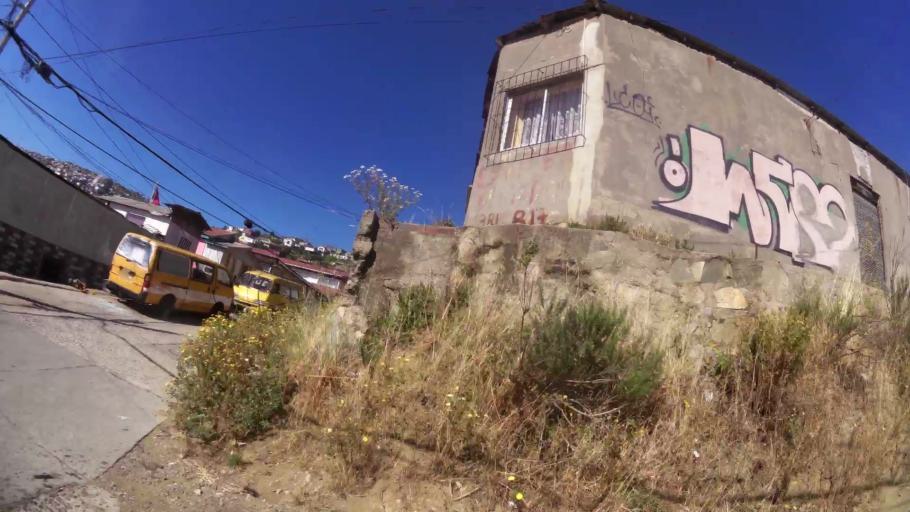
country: CL
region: Valparaiso
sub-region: Provincia de Valparaiso
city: Valparaiso
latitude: -33.0448
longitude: -71.6383
